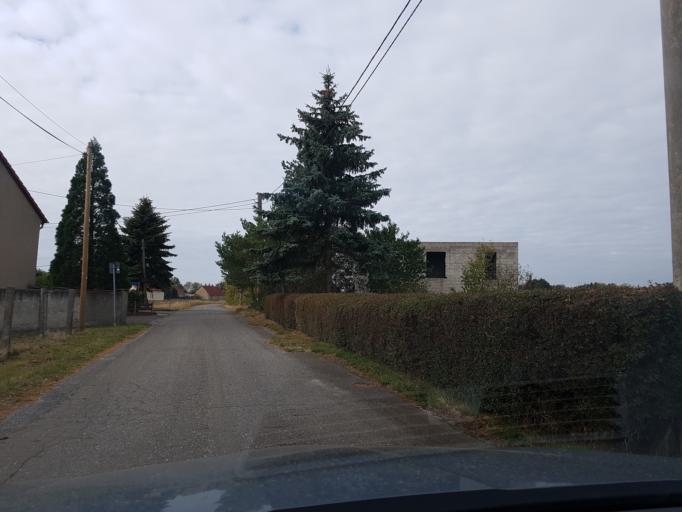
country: DE
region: Brandenburg
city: Falkenberg
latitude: 51.5545
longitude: 13.2971
